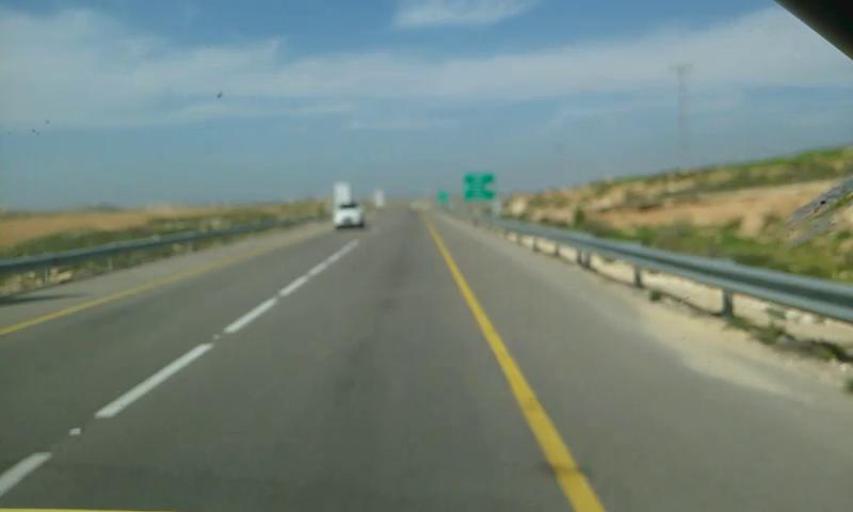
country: PS
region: West Bank
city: Az Zahiriyah
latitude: 31.3804
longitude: 35.0047
